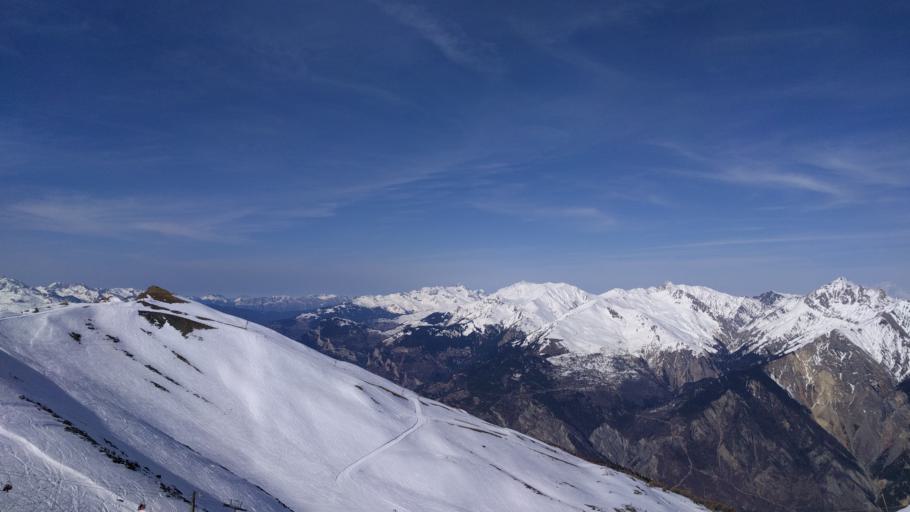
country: FR
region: Rhone-Alpes
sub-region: Departement de la Savoie
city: Valloire
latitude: 45.2058
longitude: 6.3892
